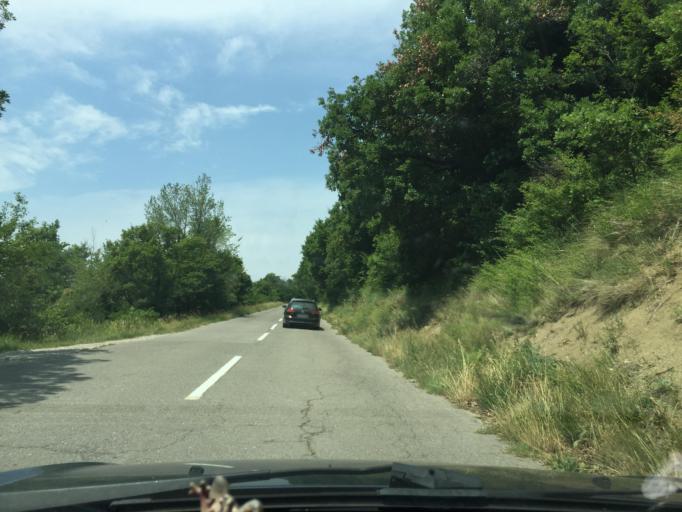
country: IT
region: Friuli Venezia Giulia
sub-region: Provincia di Trieste
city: Dolina
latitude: 45.5865
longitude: 13.8635
